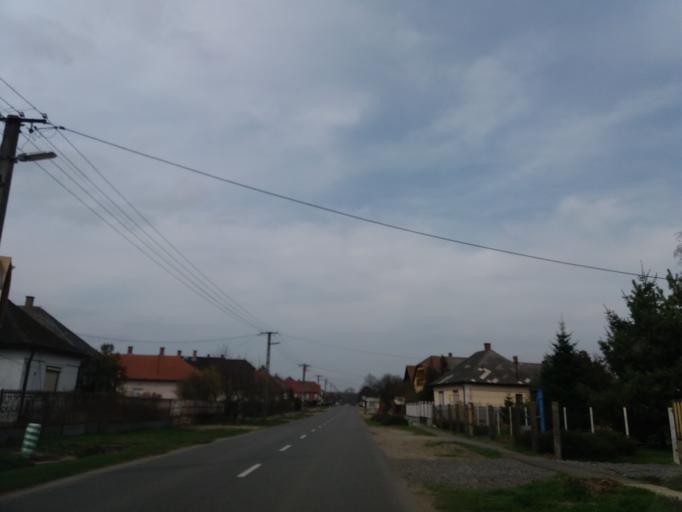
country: HU
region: Szabolcs-Szatmar-Bereg
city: Anarcs
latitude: 48.1797
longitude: 22.1007
